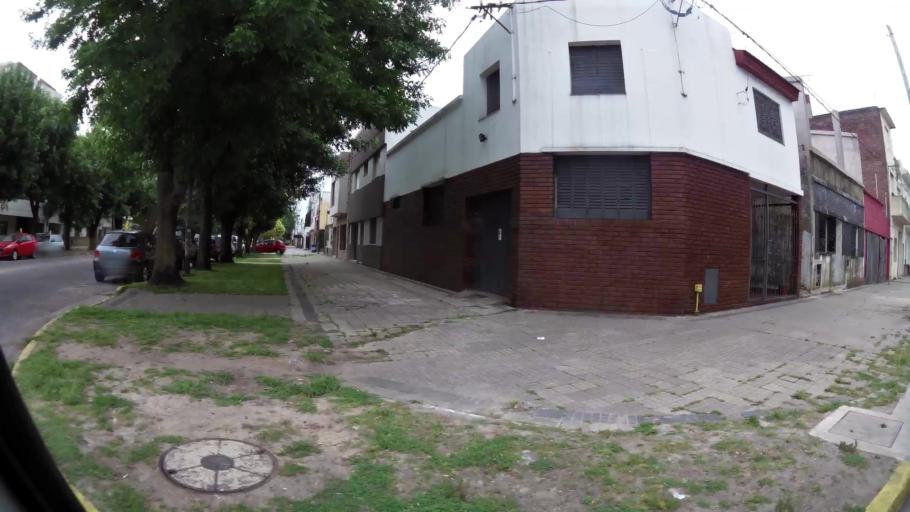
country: AR
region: Buenos Aires
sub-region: Partido de La Plata
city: La Plata
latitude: -34.9419
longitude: -57.9544
